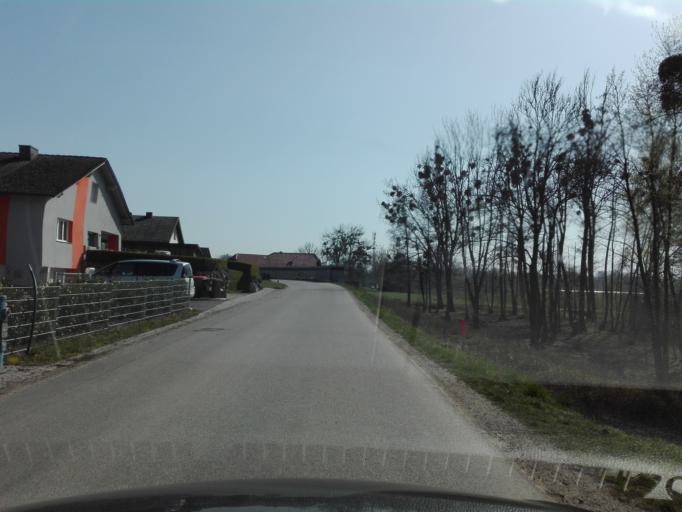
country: AT
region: Upper Austria
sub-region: Politischer Bezirk Perg
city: Perg
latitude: 48.2320
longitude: 14.5996
